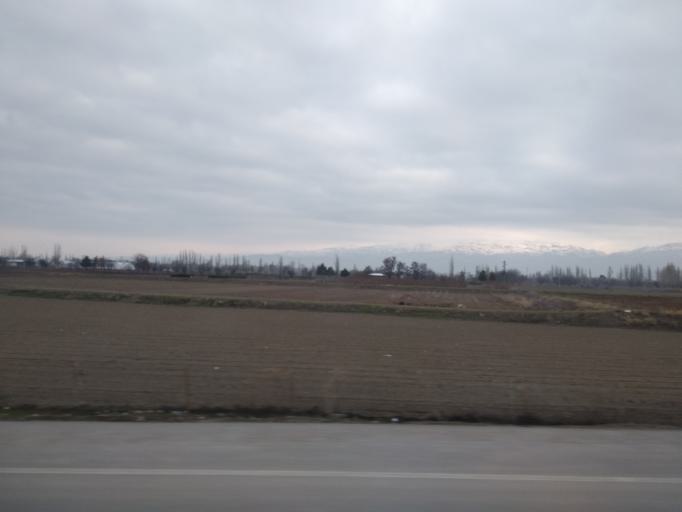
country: TR
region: Erzincan
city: Erzincan
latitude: 39.7206
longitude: 39.4878
